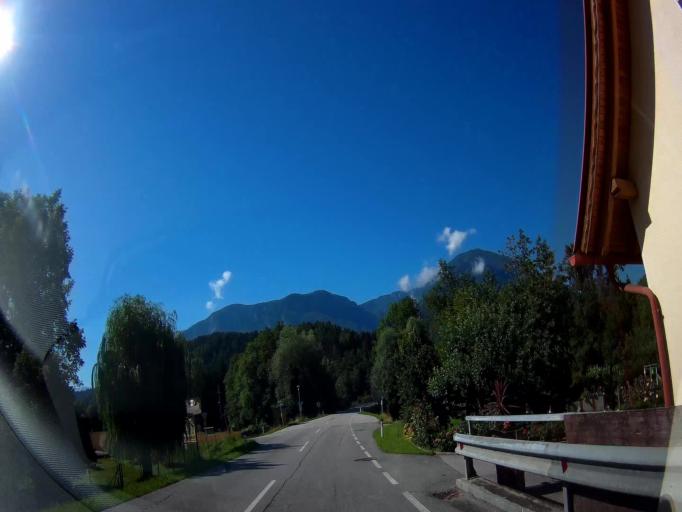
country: AT
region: Carinthia
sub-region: Politischer Bezirk Volkermarkt
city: Gallizien
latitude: 46.5715
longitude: 14.5073
